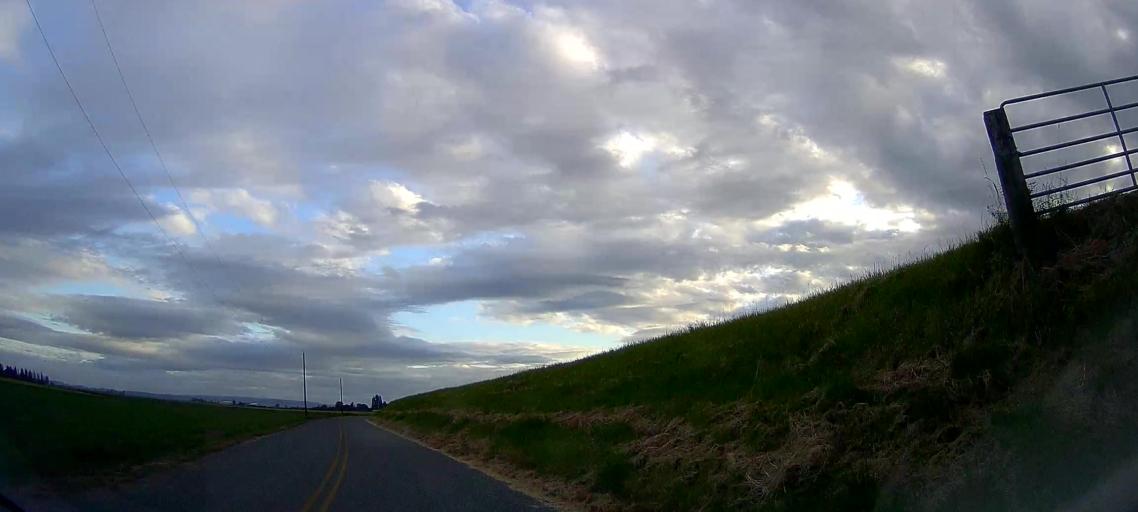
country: US
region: Washington
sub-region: Skagit County
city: Mount Vernon
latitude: 48.3700
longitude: -122.3938
